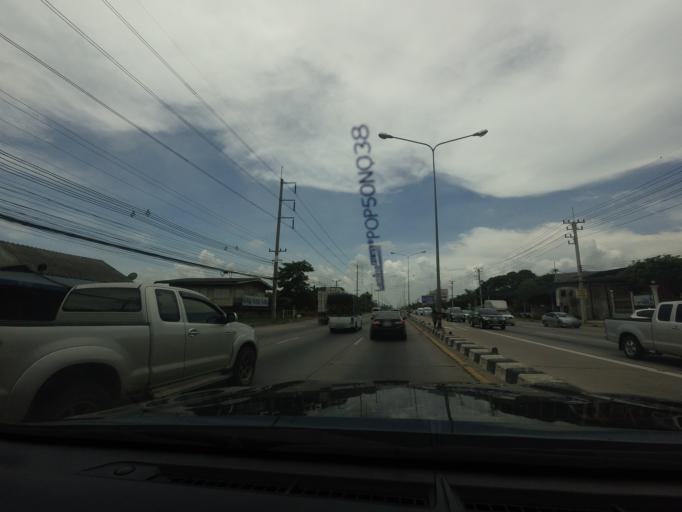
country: TH
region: Nakhon Pathom
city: Nakhon Pathom
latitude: 13.8449
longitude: 100.0243
